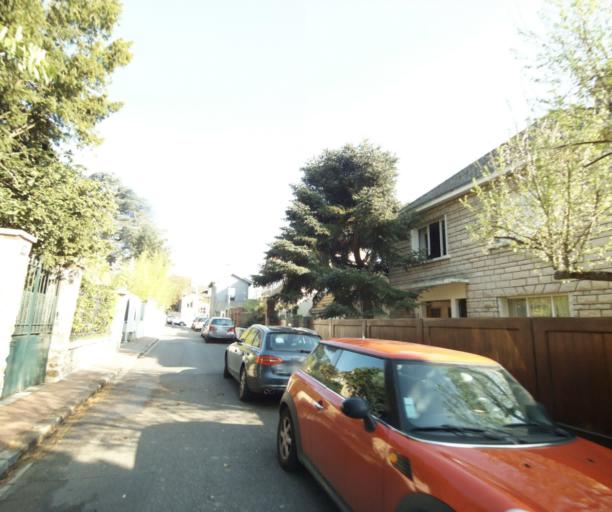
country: FR
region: Ile-de-France
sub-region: Departement des Hauts-de-Seine
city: Sevres
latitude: 48.8278
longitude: 2.2083
